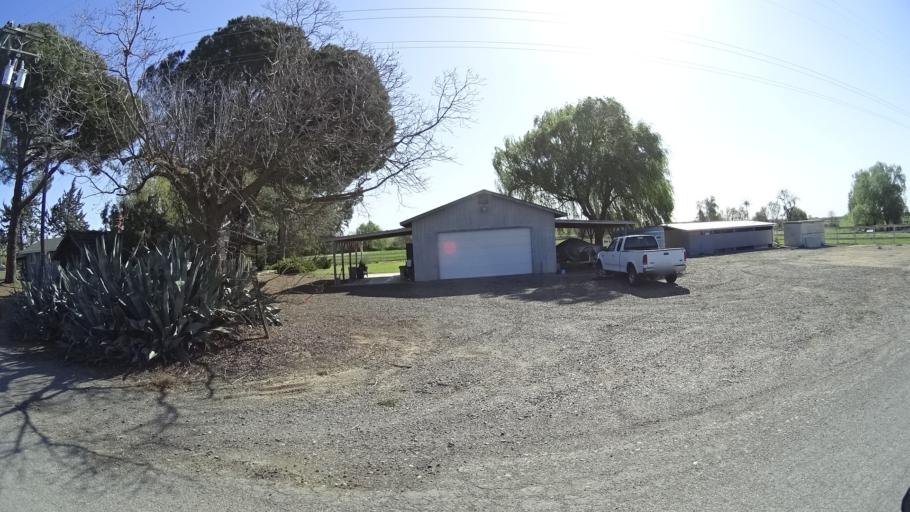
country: US
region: California
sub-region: Glenn County
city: Hamilton City
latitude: 39.7820
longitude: -122.0477
